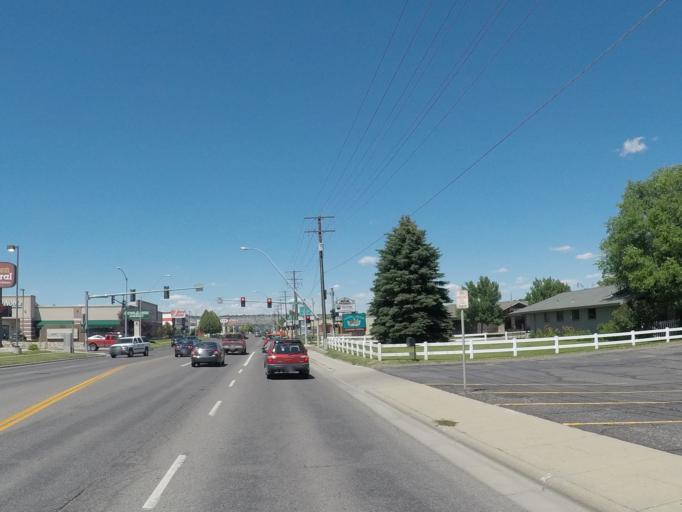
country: US
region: Montana
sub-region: Yellowstone County
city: Billings
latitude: 45.7591
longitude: -108.5761
